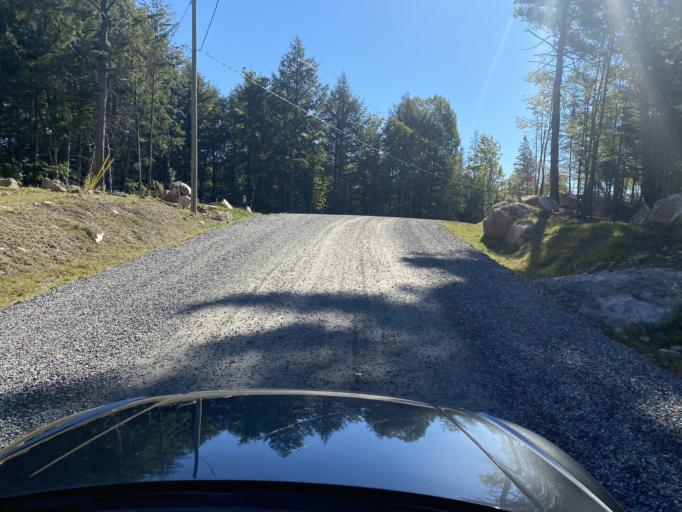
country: CA
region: Quebec
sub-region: Outaouais
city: Wakefield
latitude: 45.6360
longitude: -75.9077
